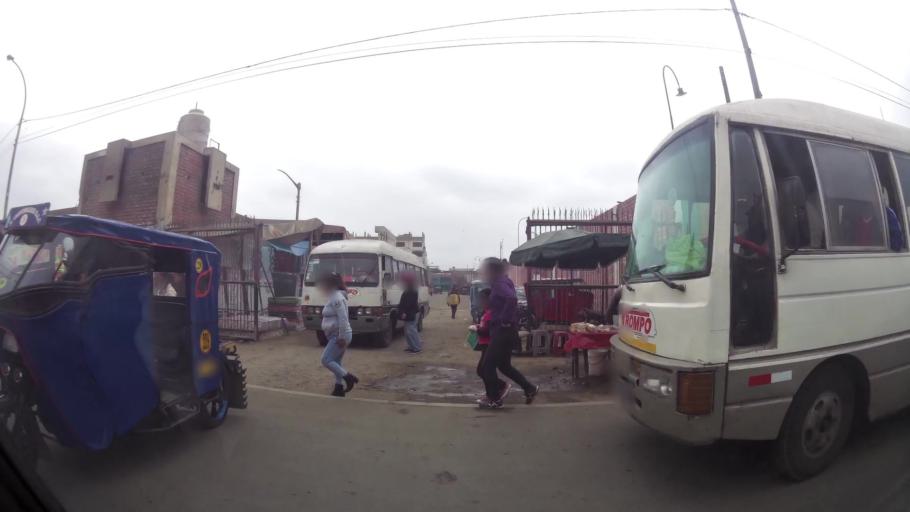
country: PE
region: Lima
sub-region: Provincia de Huaral
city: Huaral
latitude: -11.5008
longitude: -77.2054
